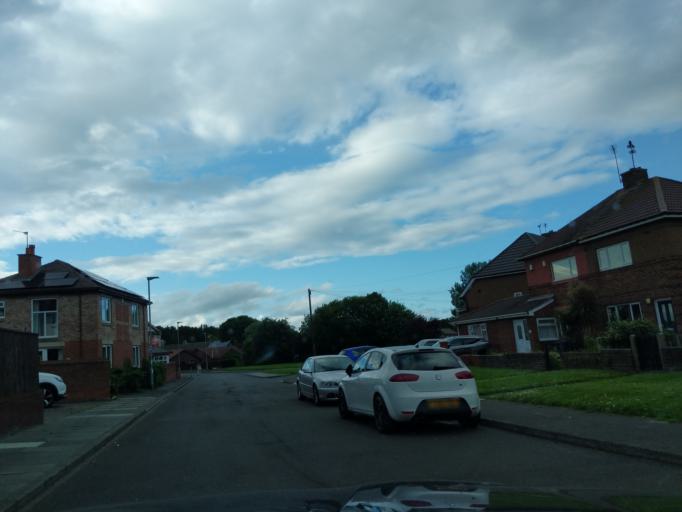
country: GB
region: England
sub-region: Northumberland
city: Seaton Delaval
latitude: 55.0854
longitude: -1.5183
